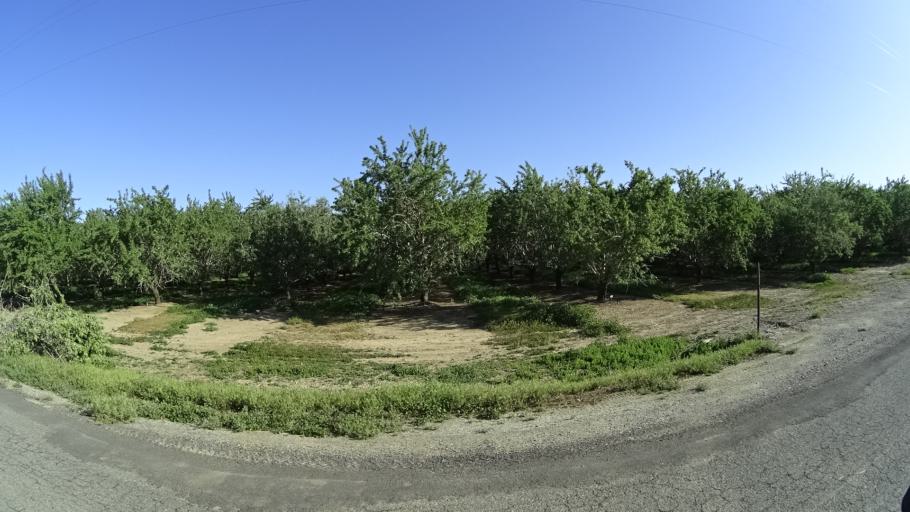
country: US
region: California
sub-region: Glenn County
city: Orland
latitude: 39.6959
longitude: -122.1069
